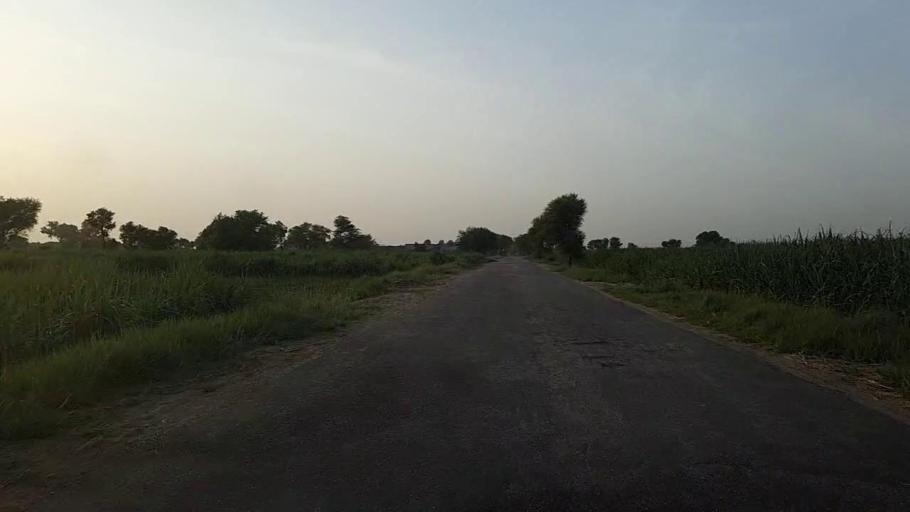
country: PK
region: Sindh
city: Ubauro
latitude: 28.2276
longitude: 69.8175
